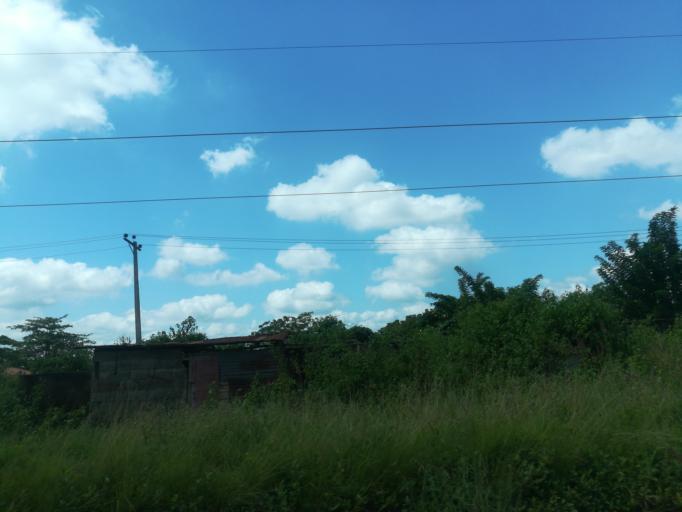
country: NG
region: Oyo
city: Ibadan
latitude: 7.3539
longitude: 3.8620
